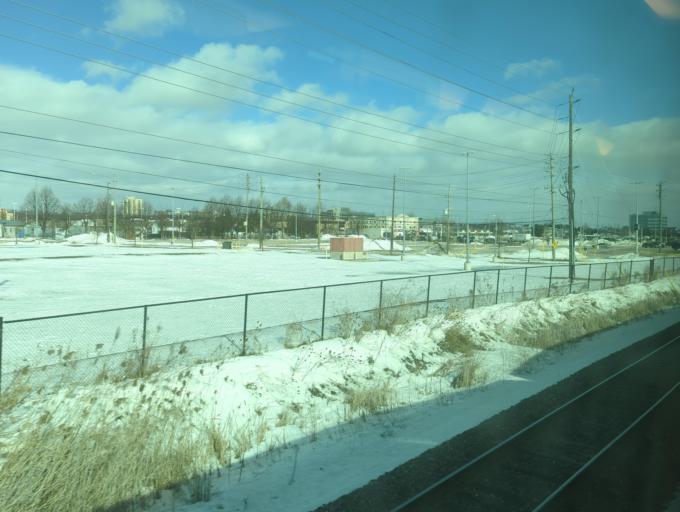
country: CA
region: Ontario
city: Oakville
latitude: 43.4525
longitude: -79.6851
